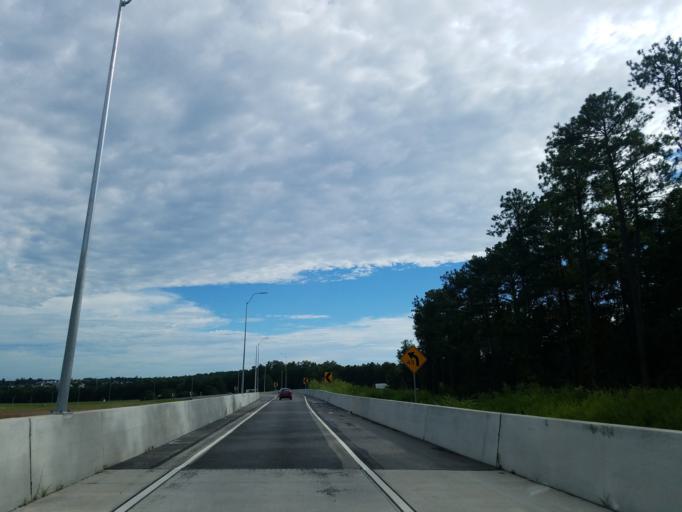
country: US
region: Georgia
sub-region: Henry County
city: Stockbridge
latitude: 33.5453
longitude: -84.2689
